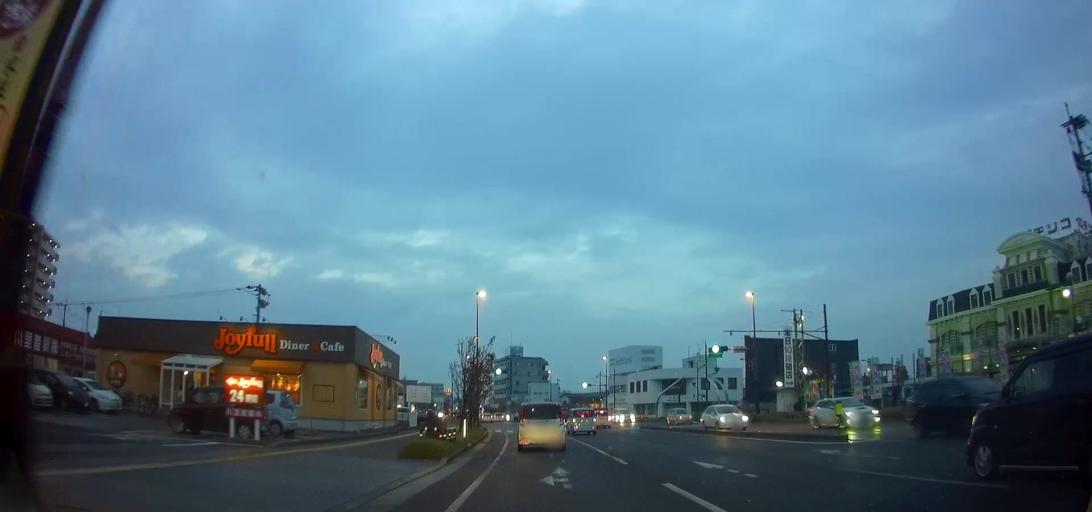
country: JP
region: Nagasaki
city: Omura
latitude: 32.9062
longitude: 129.9569
